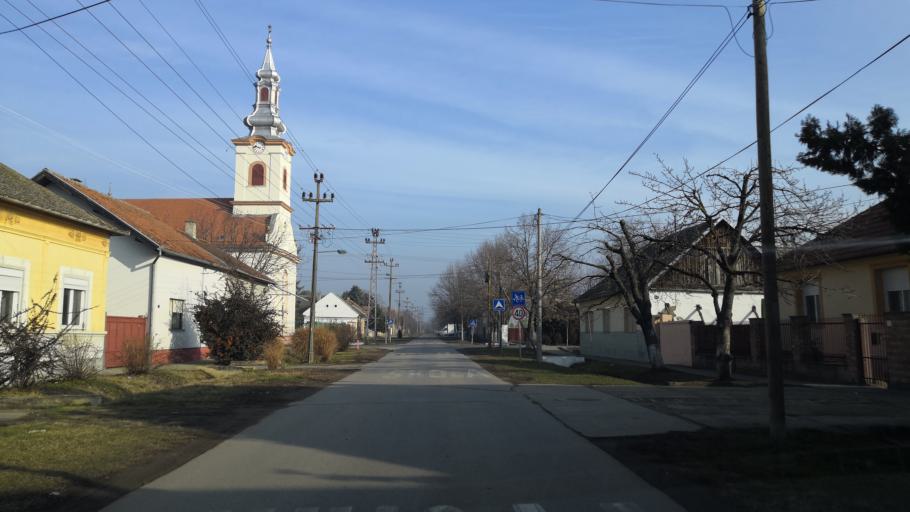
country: RS
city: Rumenka
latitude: 45.2951
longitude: 19.7464
